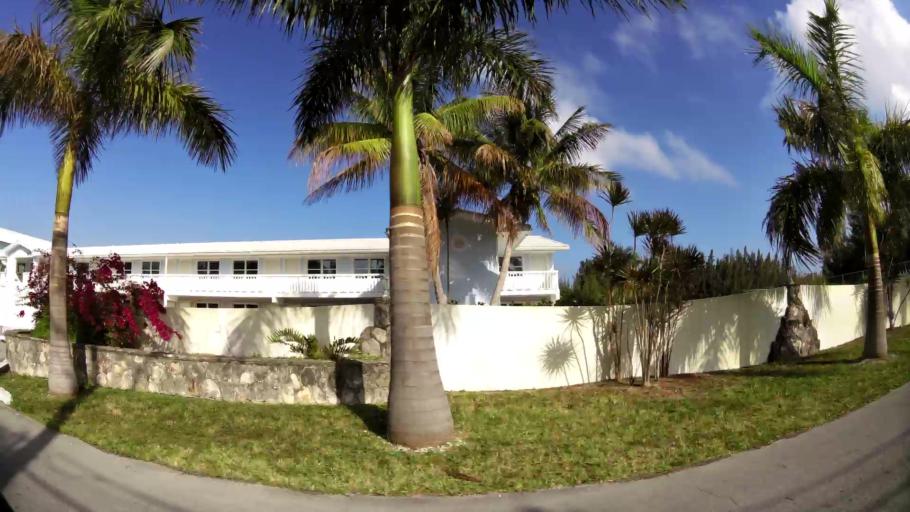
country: BS
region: Freeport
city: Lucaya
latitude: 26.5058
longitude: -78.6584
